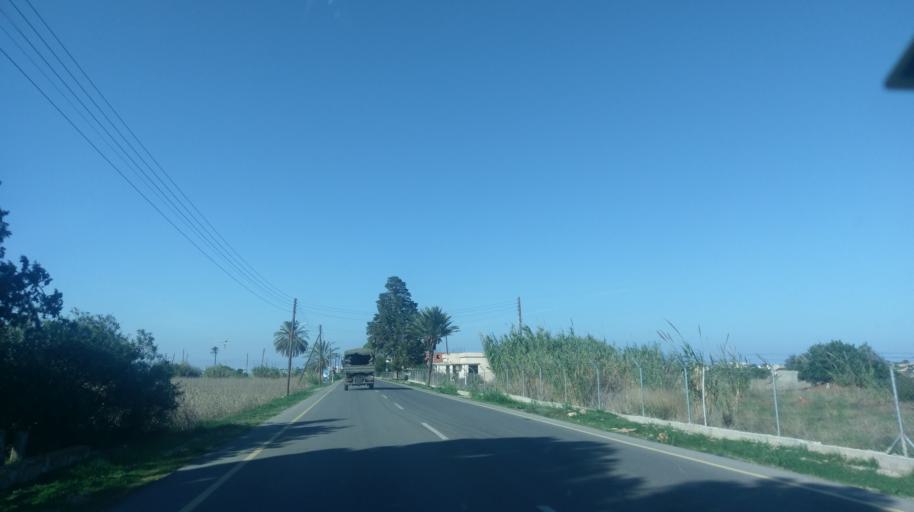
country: CY
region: Ammochostos
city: Deryneia
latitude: 35.0865
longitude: 33.9549
